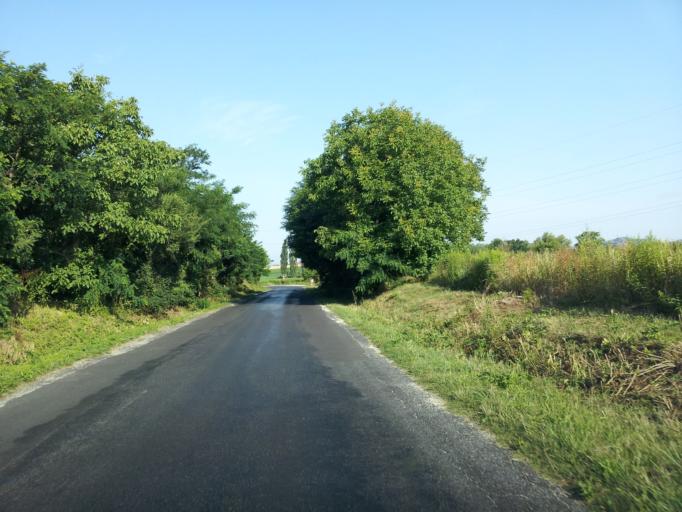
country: HU
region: Zala
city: Gyenesdias
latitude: 46.8573
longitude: 17.3169
